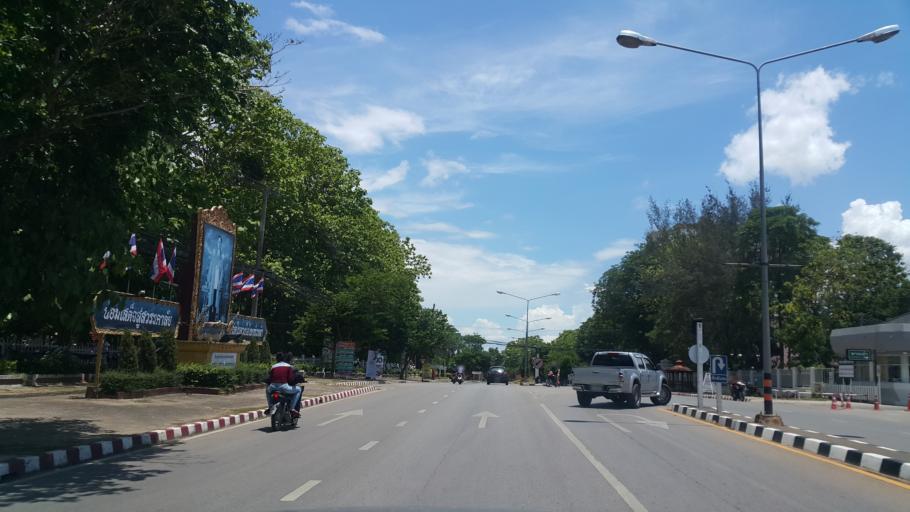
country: TH
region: Phayao
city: Phayao
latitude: 19.1905
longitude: 99.8783
